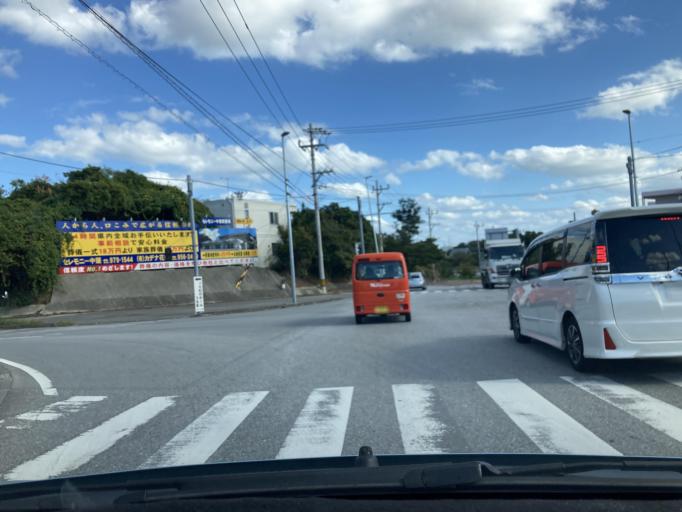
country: JP
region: Okinawa
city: Gushikawa
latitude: 26.3733
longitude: 127.8269
